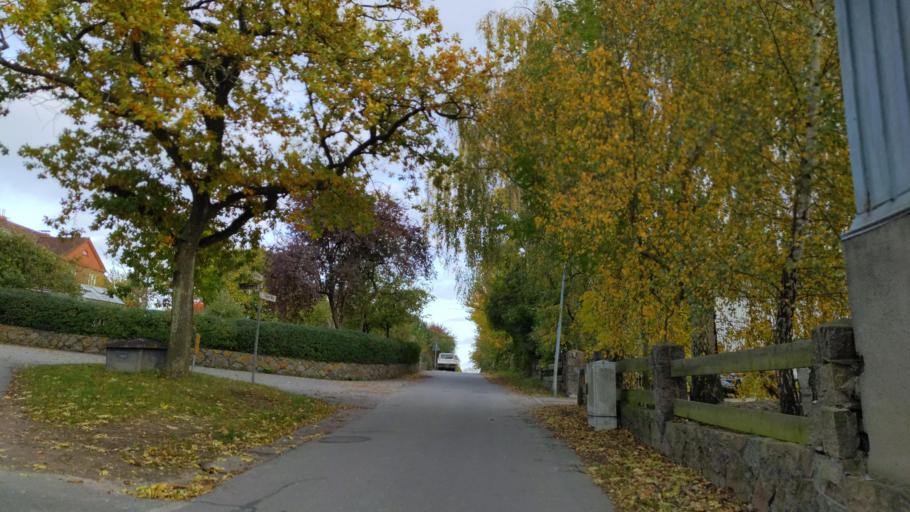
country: DE
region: Schleswig-Holstein
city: Sierksdorf
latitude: 54.0999
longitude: 10.7690
